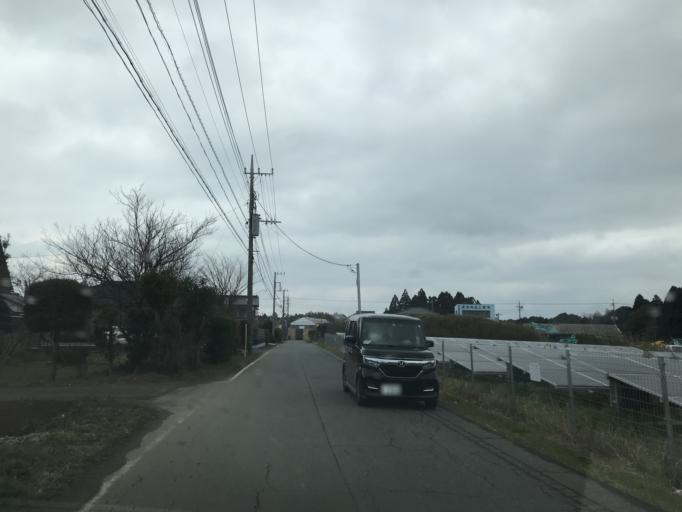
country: JP
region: Chiba
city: Sawara
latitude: 35.8591
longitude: 140.5503
